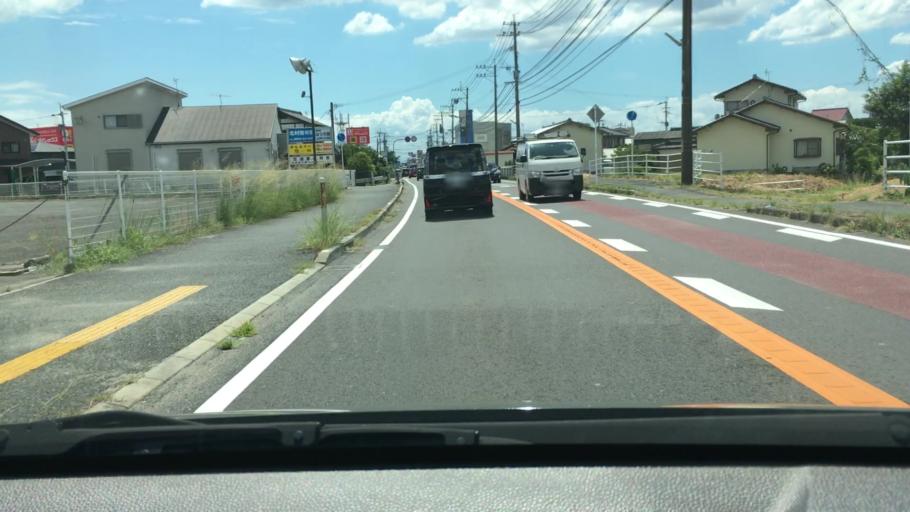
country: JP
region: Saga Prefecture
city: Kanzakimachi-kanzaki
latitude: 33.3184
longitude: 130.3820
